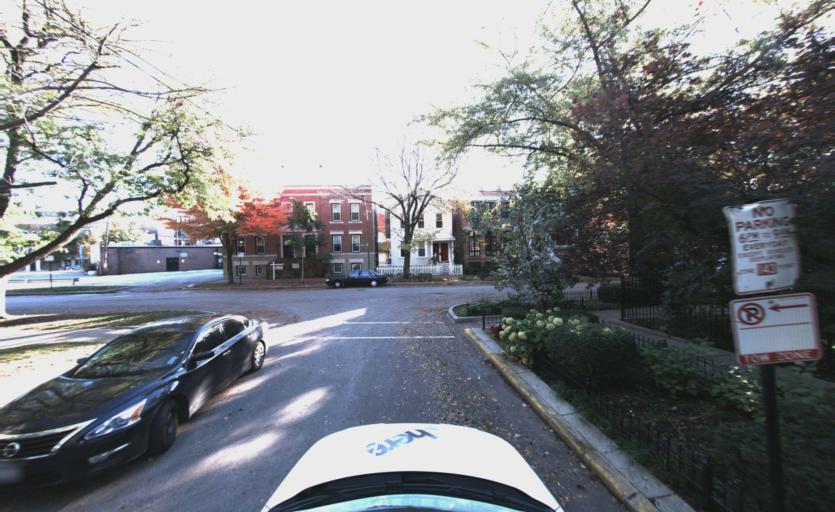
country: US
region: Illinois
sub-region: Cook County
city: Chicago
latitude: 41.9299
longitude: -87.6564
